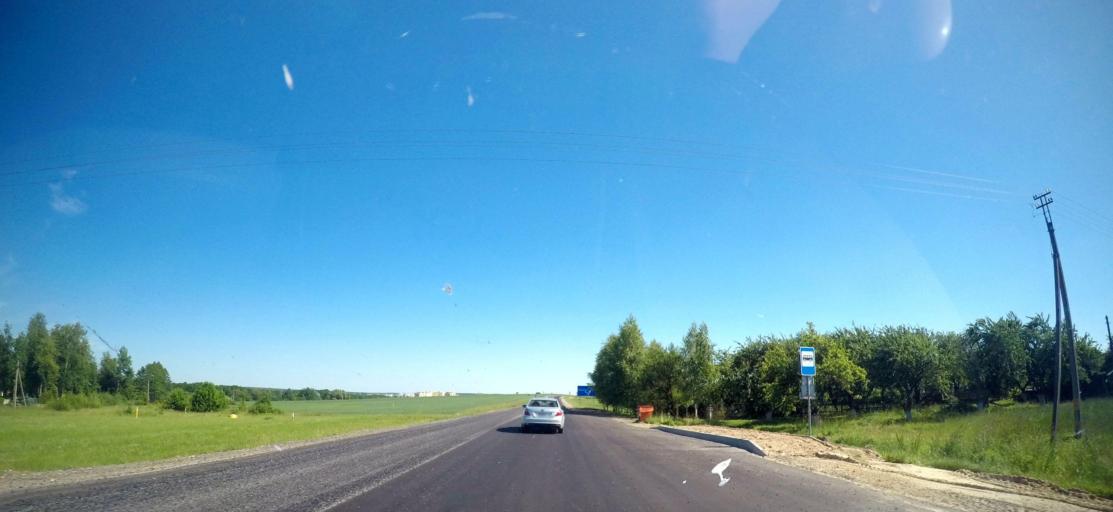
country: BY
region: Grodnenskaya
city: Vyalikaya Byerastavitsa
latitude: 53.2117
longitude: 24.0035
